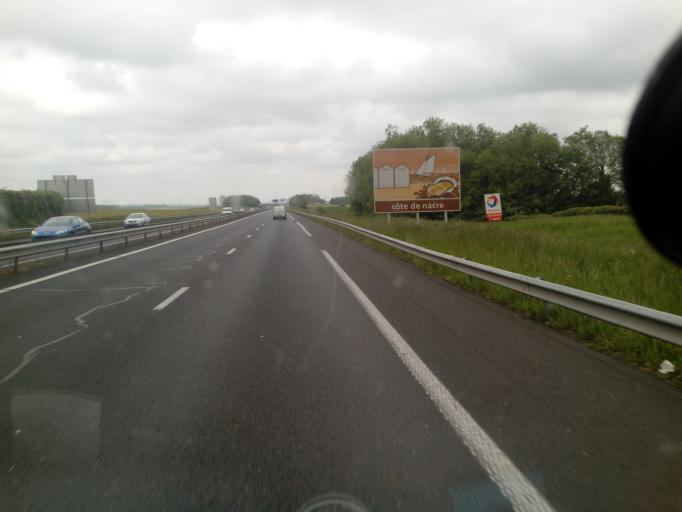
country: FR
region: Lower Normandy
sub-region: Departement du Calvados
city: Mouen
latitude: 49.1565
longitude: -0.4797
